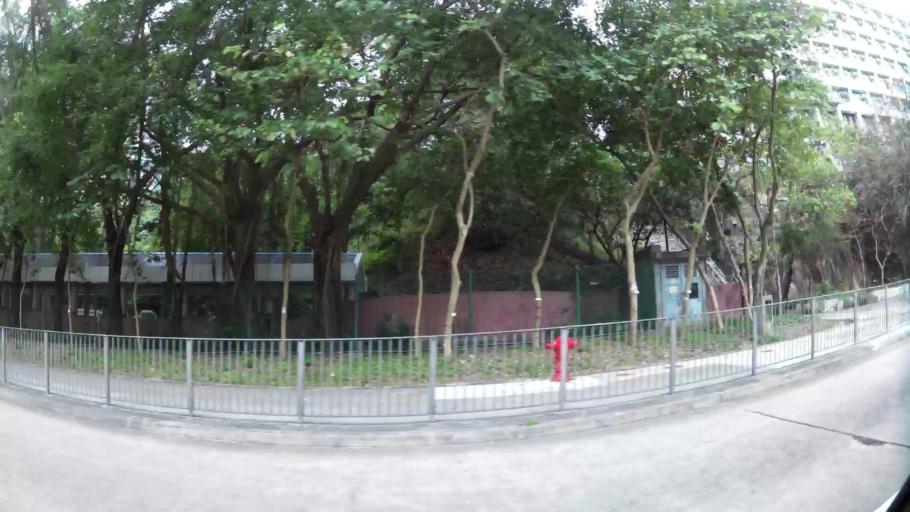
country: HK
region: Wanchai
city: Wan Chai
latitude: 22.2675
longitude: 114.2376
